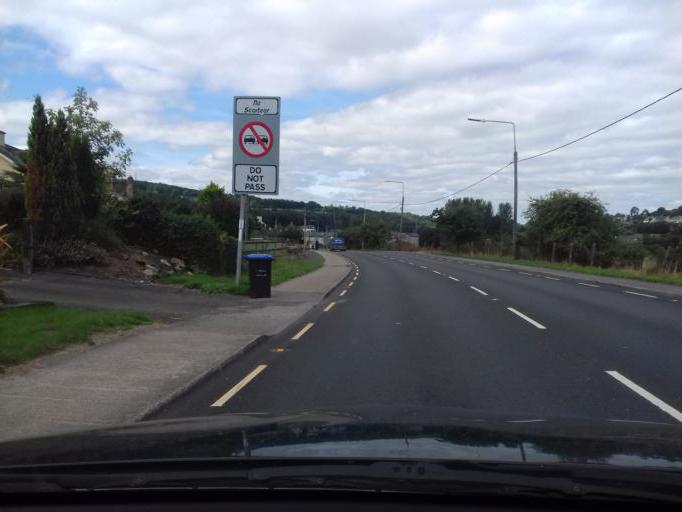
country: IE
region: Leinster
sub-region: Wicklow
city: Baltinglass
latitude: 52.9371
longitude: -6.7084
